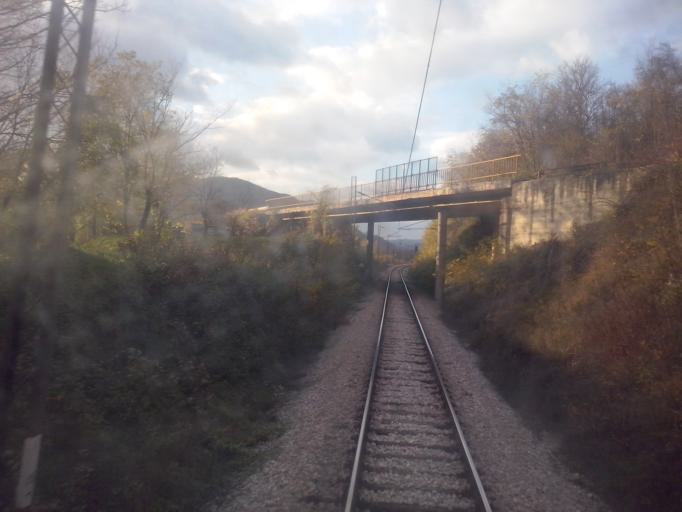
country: RS
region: Central Serbia
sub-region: Zlatiborski Okrug
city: Kosjeric
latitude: 43.9908
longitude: 19.9219
